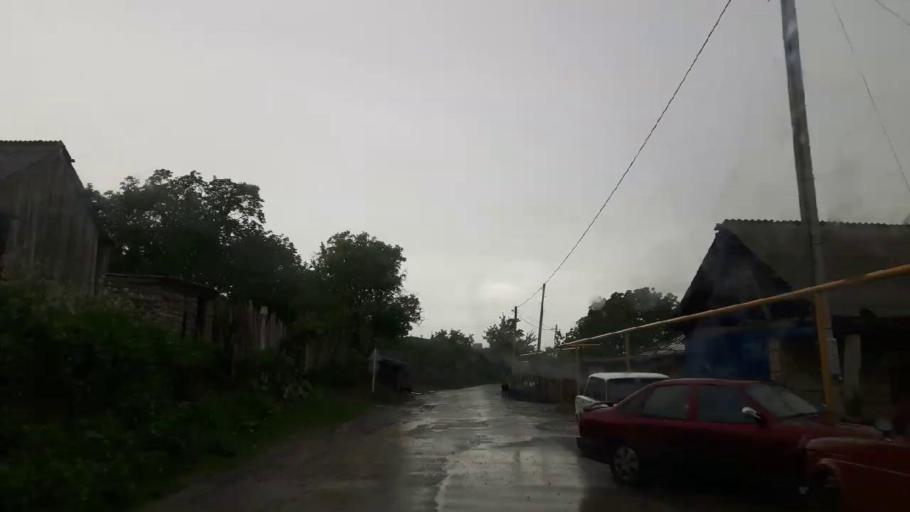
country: GE
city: Agara
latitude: 42.0175
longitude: 43.8429
